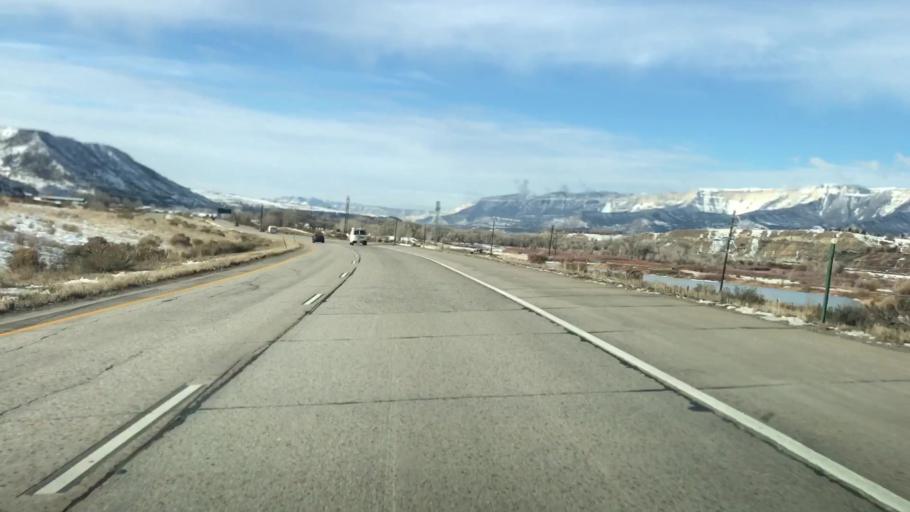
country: US
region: Colorado
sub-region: Garfield County
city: Rifle
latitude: 39.5301
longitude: -107.7390
